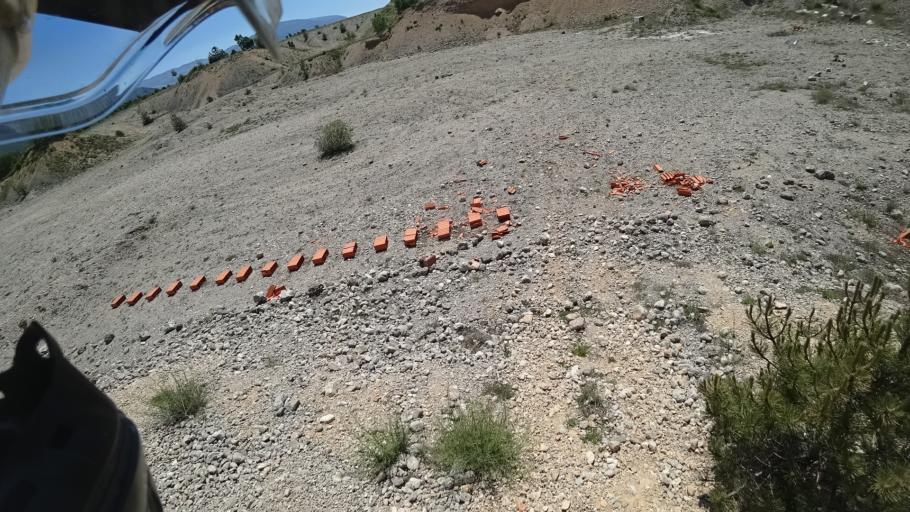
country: HR
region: Sibensko-Kniniska
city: Knin
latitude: 44.0152
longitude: 16.3447
